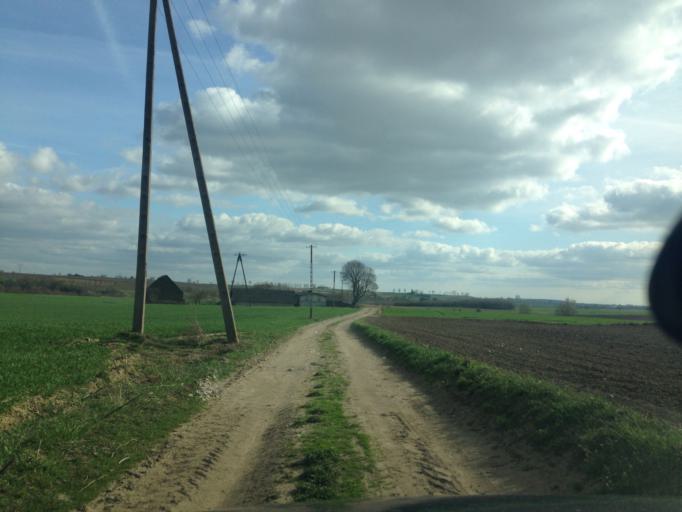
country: PL
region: Kujawsko-Pomorskie
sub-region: Powiat brodnicki
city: Bartniczka
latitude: 53.2485
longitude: 19.5774
